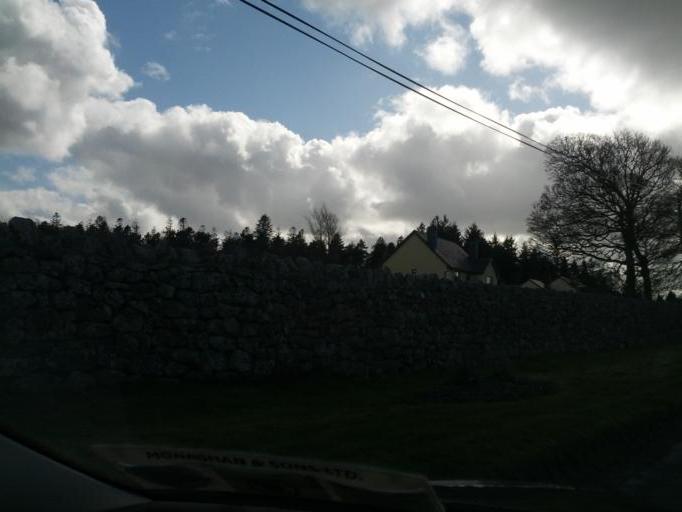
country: IE
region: Connaught
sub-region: County Galway
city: Athenry
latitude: 53.3763
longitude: -8.6990
